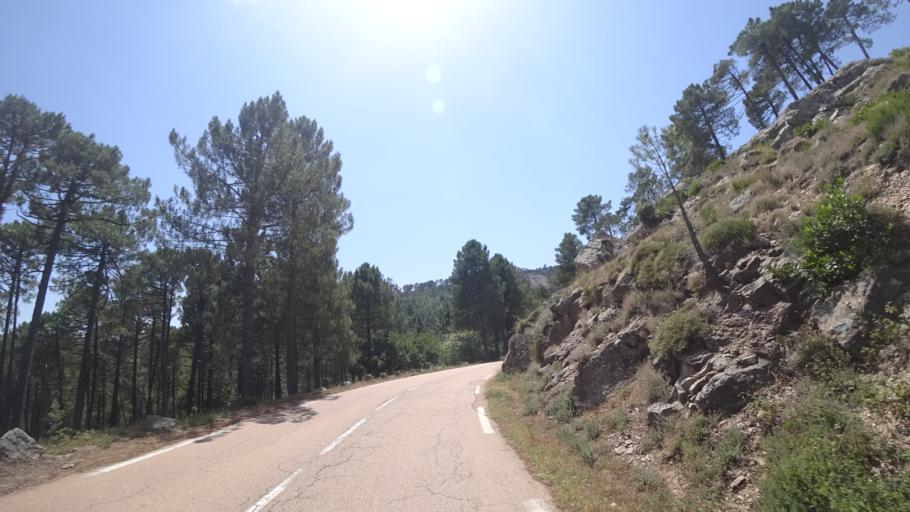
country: FR
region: Corsica
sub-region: Departement de la Corse-du-Sud
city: Zonza
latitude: 41.6792
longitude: 9.2031
